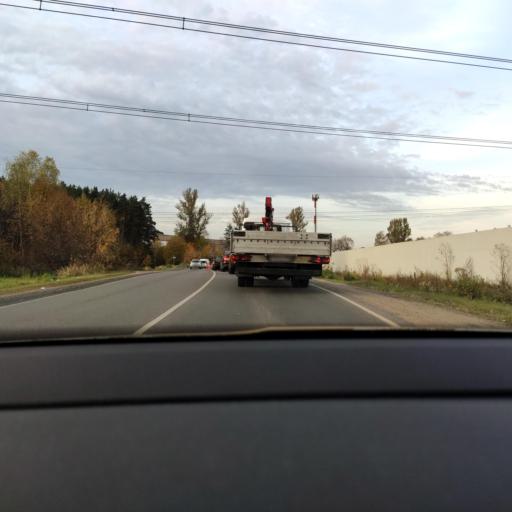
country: RU
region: Moskovskaya
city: Cherkizovo
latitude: 55.9699
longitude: 37.7654
